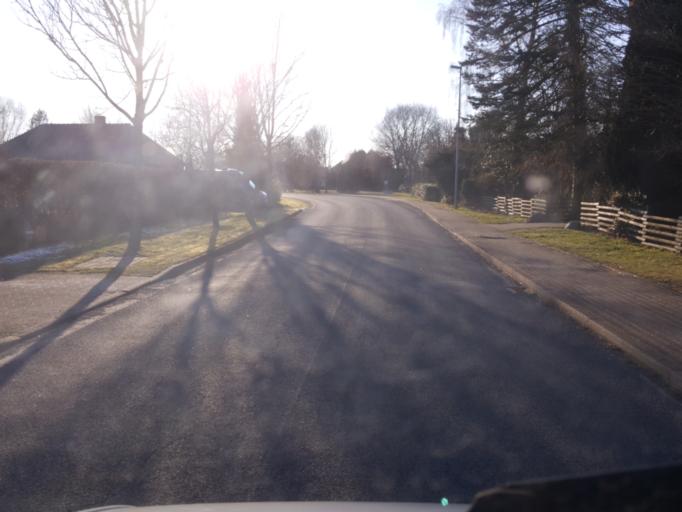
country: DE
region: North Rhine-Westphalia
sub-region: Regierungsbezirk Detmold
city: Hille
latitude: 52.4238
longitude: 8.7303
